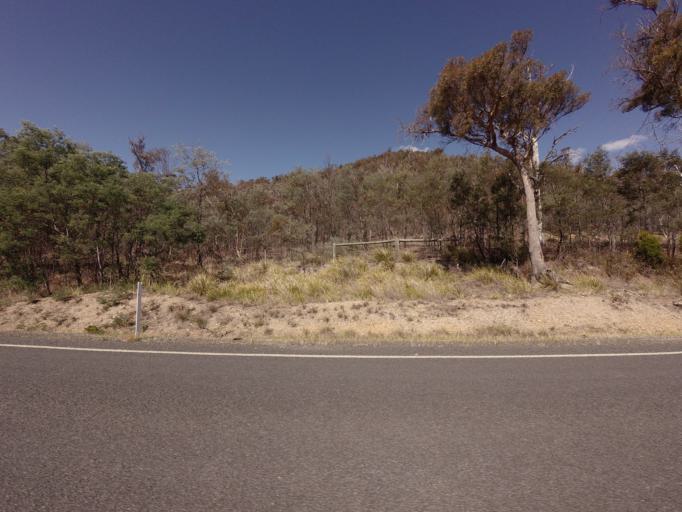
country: AU
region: Tasmania
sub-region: Break O'Day
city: St Helens
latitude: -41.6846
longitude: 147.8829
